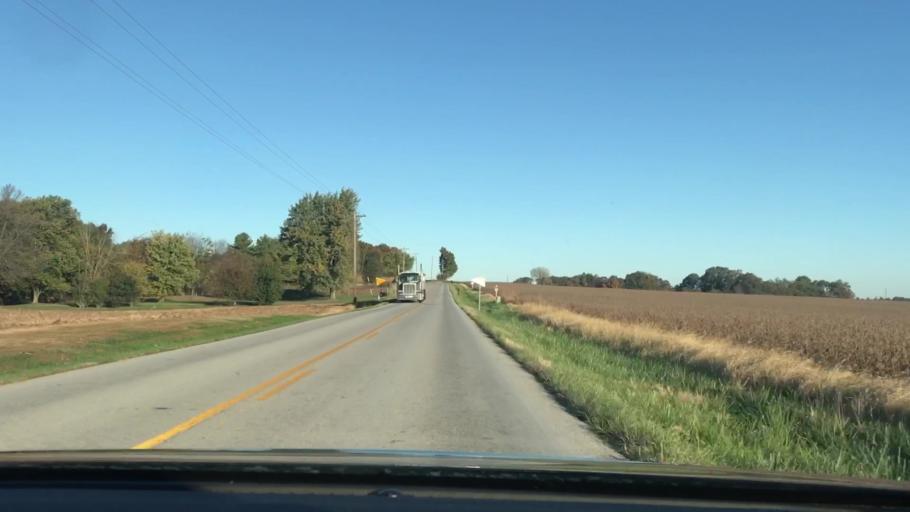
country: US
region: Kentucky
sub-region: Simpson County
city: Franklin
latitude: 36.7776
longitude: -86.6190
